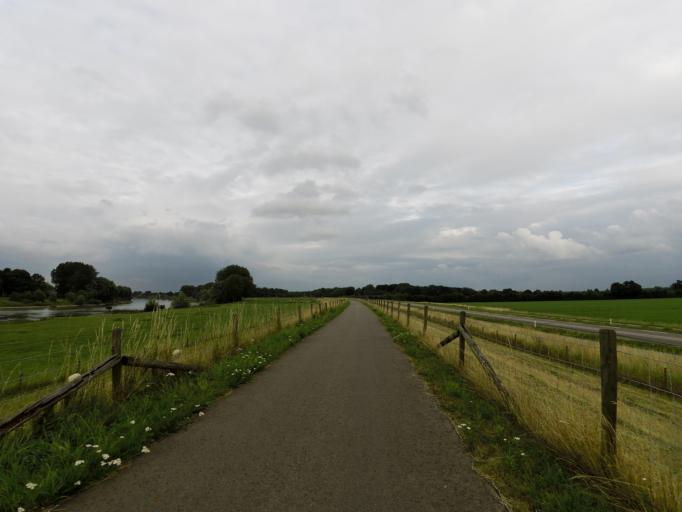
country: NL
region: Gelderland
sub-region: Gemeente Rheden
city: De Steeg
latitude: 51.9920
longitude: 6.0882
